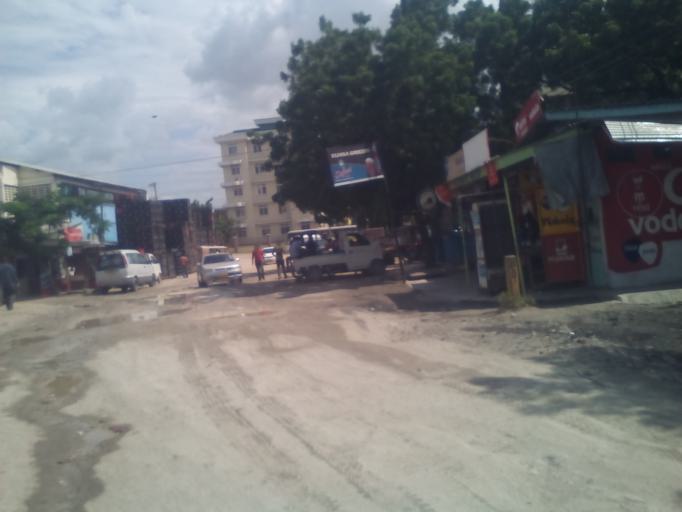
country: TZ
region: Dar es Salaam
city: Dar es Salaam
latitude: -6.8436
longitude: 39.2744
